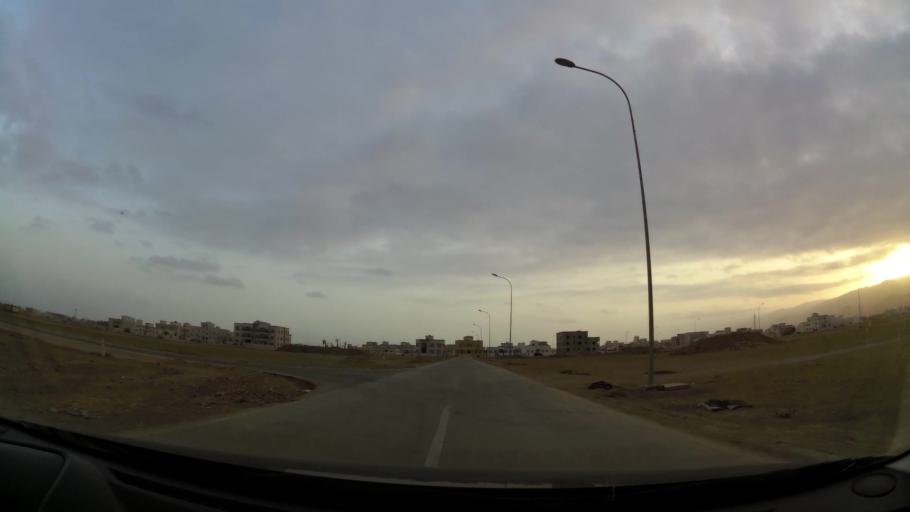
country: OM
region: Zufar
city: Salalah
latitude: 17.0281
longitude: 54.0156
